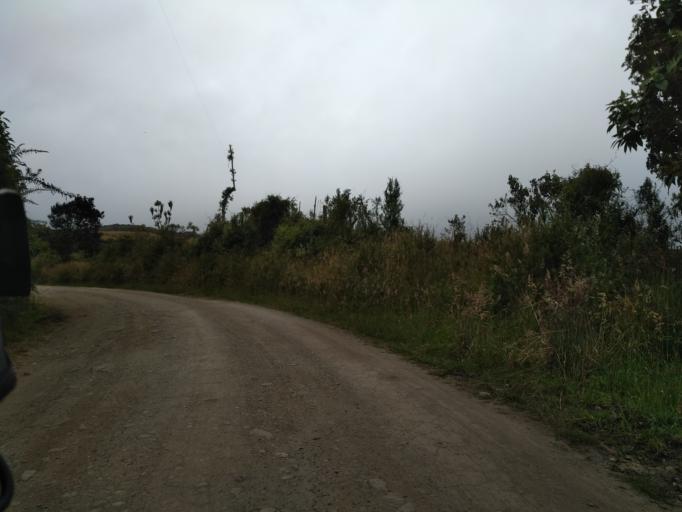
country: EC
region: Carchi
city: Tulcan
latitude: 0.7447
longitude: -77.7819
